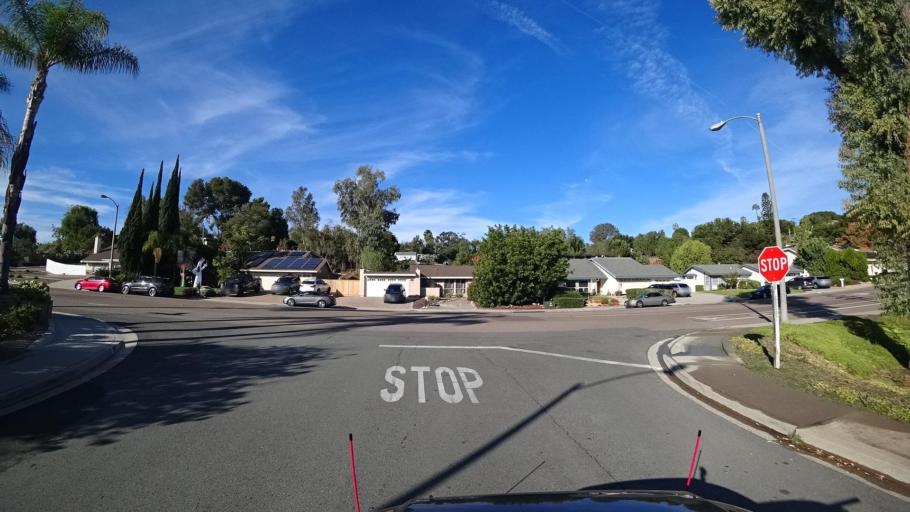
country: US
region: California
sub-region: San Diego County
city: Spring Valley
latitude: 32.7350
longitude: -116.9831
